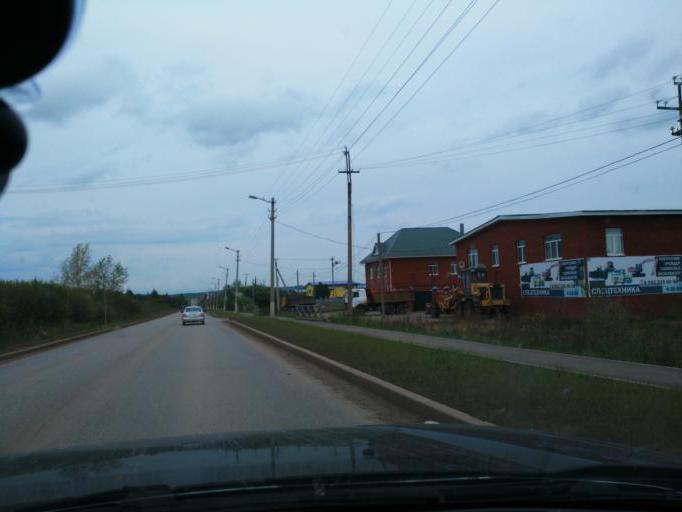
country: RU
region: Perm
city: Chernushka
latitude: 56.5367
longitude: 56.0984
